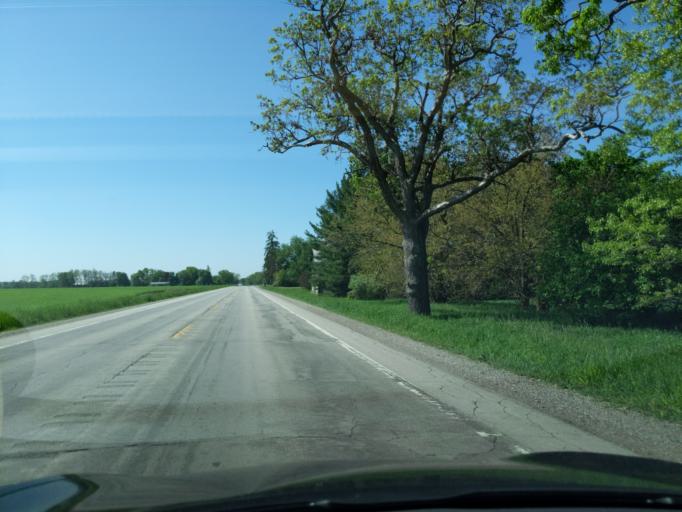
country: US
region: Michigan
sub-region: Ingham County
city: Stockbridge
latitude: 42.5069
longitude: -84.1901
